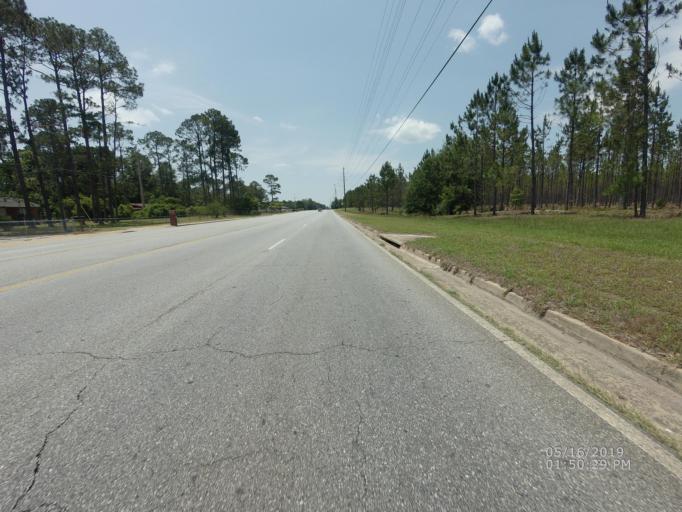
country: US
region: Georgia
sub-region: Dougherty County
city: Albany
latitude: 31.5492
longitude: -84.1940
